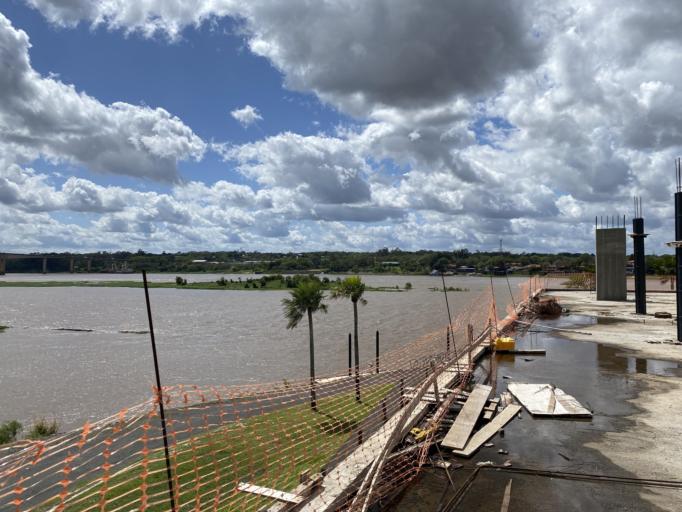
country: PY
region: Central
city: Colonia Mariano Roque Alonso
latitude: -25.1872
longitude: -57.5563
